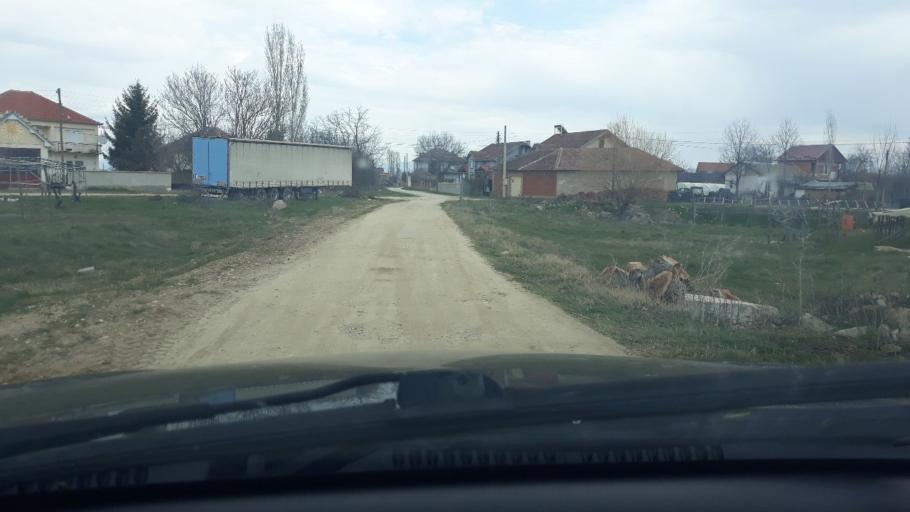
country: MK
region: Krusevo
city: Bucin
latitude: 41.2794
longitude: 21.3370
